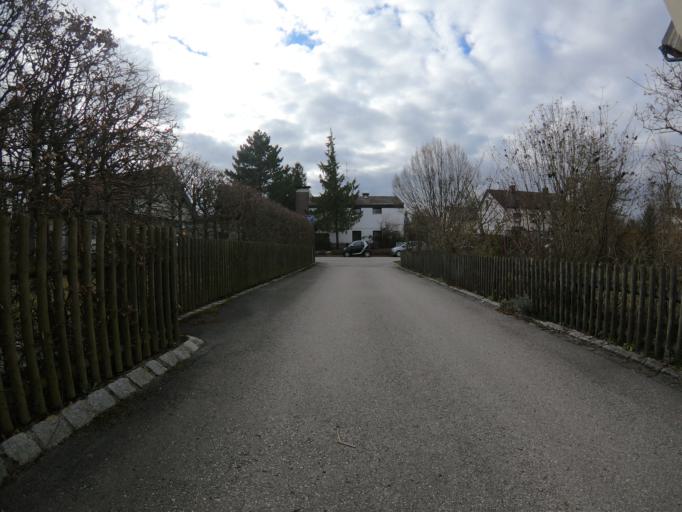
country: DE
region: Bavaria
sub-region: Upper Bavaria
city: Fuerstenfeldbruck
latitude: 48.1833
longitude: 11.2659
